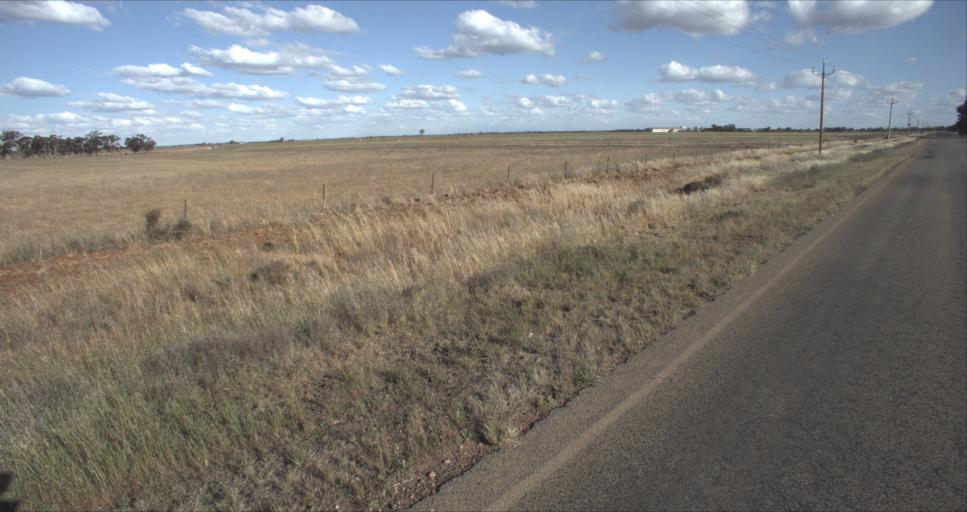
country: AU
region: New South Wales
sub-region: Leeton
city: Leeton
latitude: -34.5382
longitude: 146.2802
